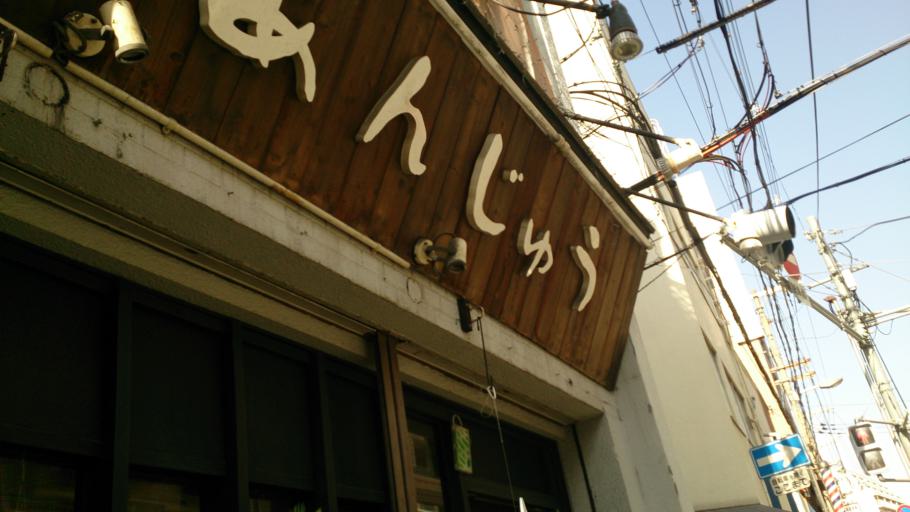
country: JP
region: Osaka
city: Osaka-shi
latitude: 34.7087
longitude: 135.5057
